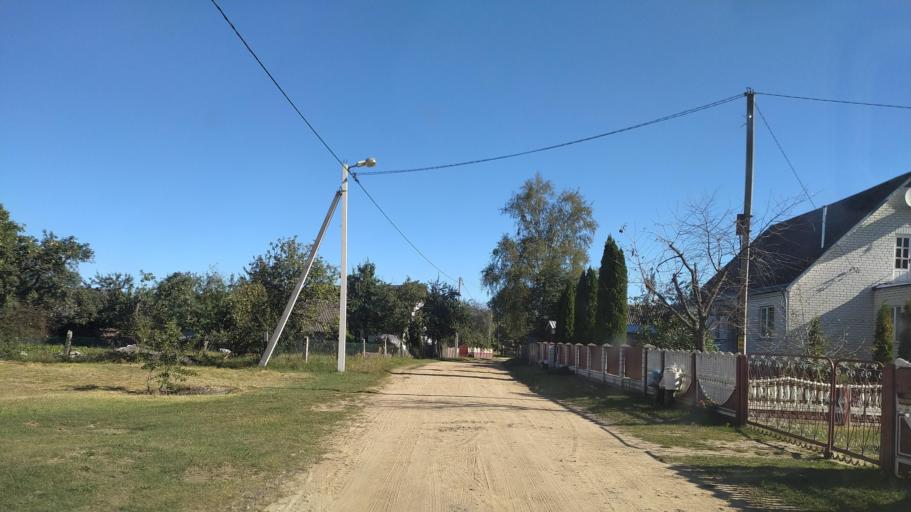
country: BY
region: Brest
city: Pruzhany
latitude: 52.4842
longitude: 24.7090
